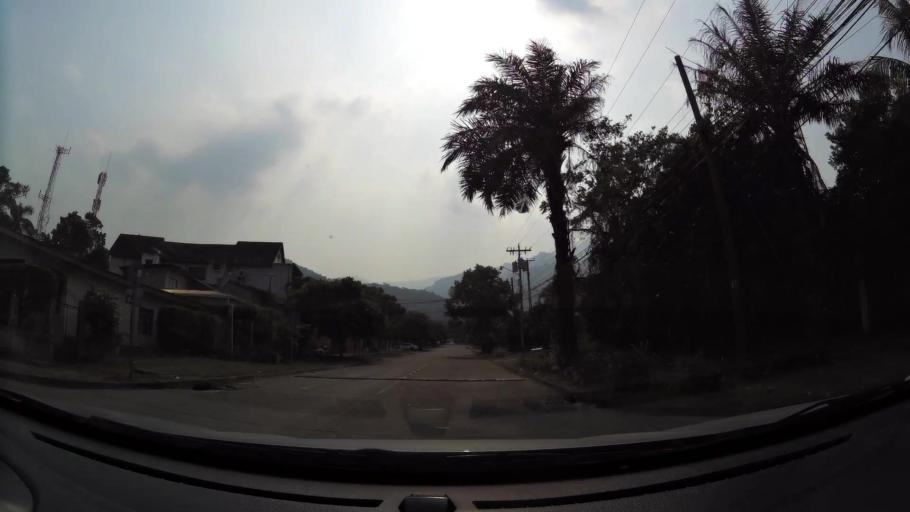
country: HN
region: Cortes
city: Armenta
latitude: 15.5010
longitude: -88.0442
